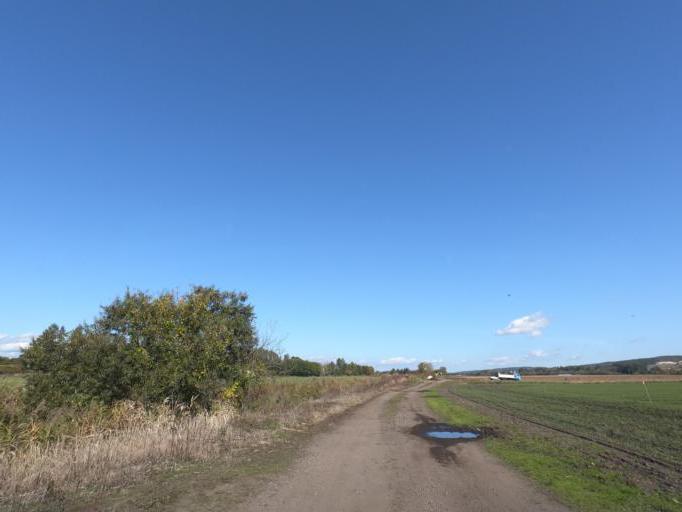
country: JP
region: Hokkaido
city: Otofuke
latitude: 43.0604
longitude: 143.2770
